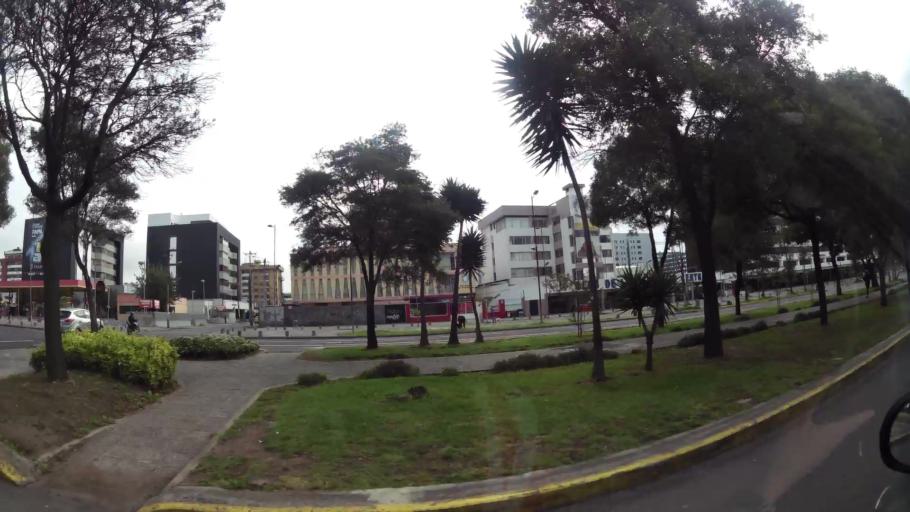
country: EC
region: Pichincha
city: Quito
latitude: -0.1755
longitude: -78.4874
